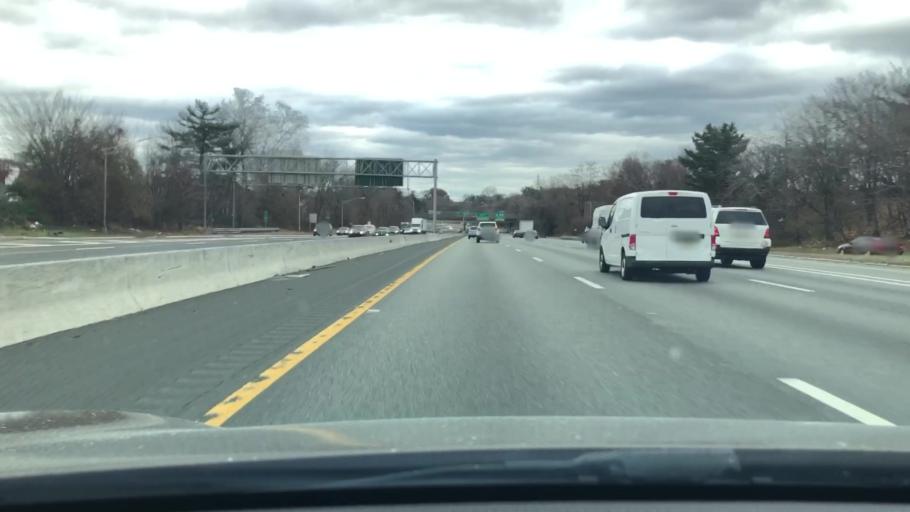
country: US
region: New Jersey
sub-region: Passaic County
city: Paterson
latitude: 40.9014
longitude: -74.1524
